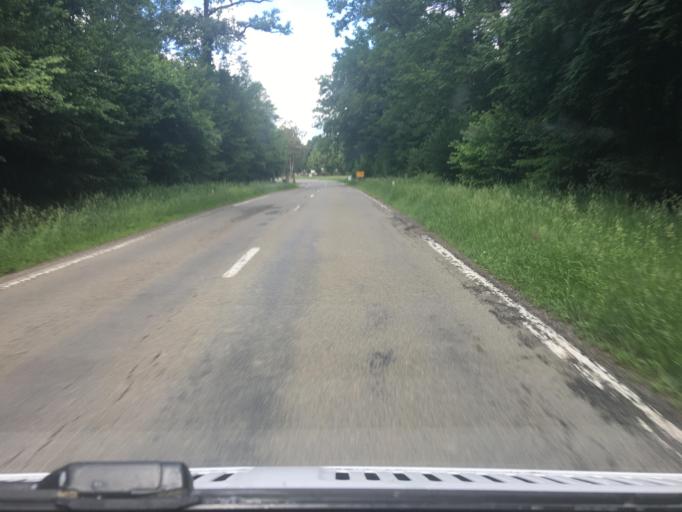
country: BE
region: Wallonia
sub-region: Province du Luxembourg
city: Florenville
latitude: 49.6806
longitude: 5.3346
